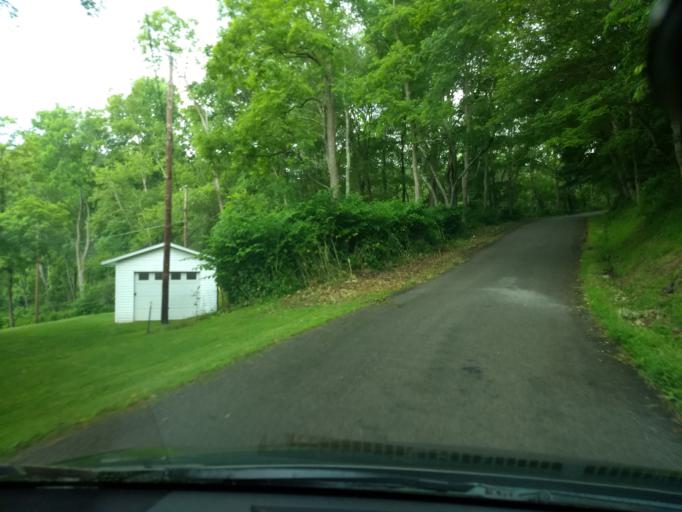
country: US
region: Pennsylvania
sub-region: Westmoreland County
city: Avonmore
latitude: 40.5260
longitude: -79.4953
